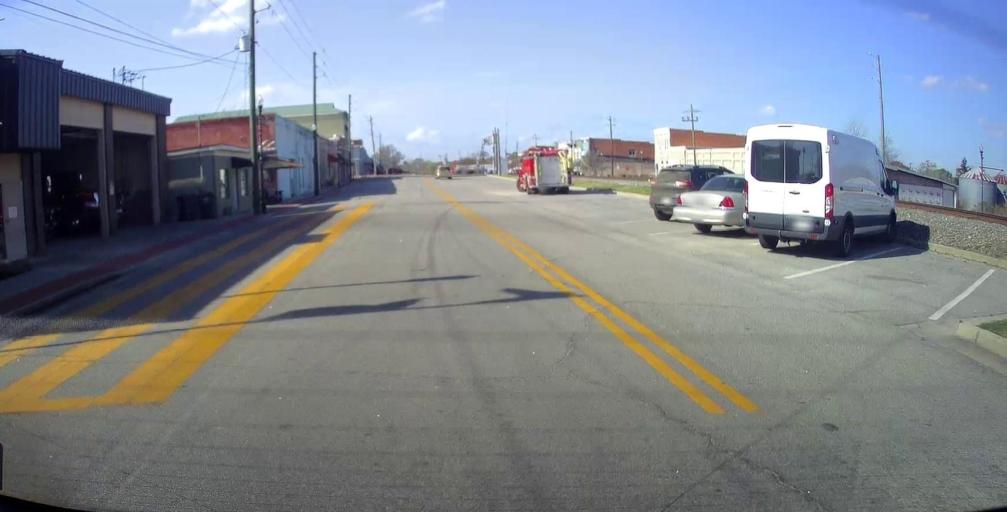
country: US
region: Georgia
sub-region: Dodge County
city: Eastman
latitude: 32.1959
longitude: -83.1750
